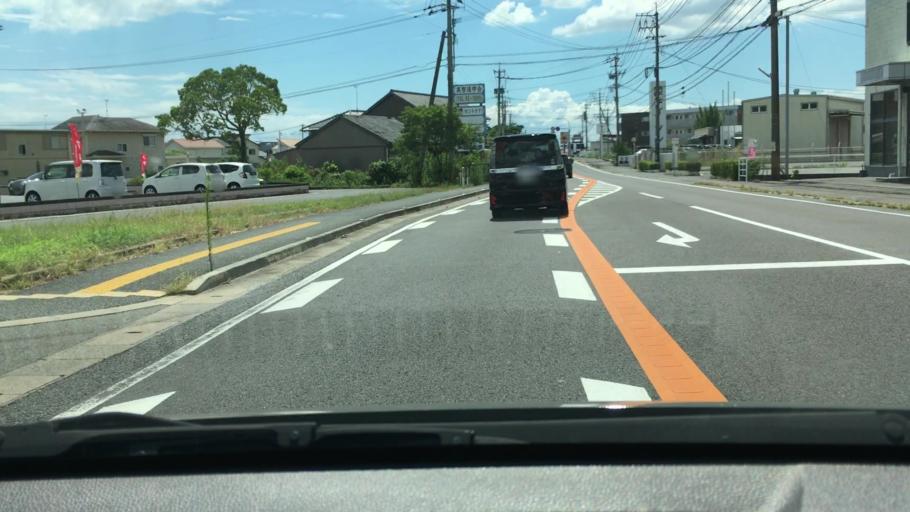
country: JP
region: Saga Prefecture
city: Kanzakimachi-kanzaki
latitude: 33.3173
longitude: 130.3806
